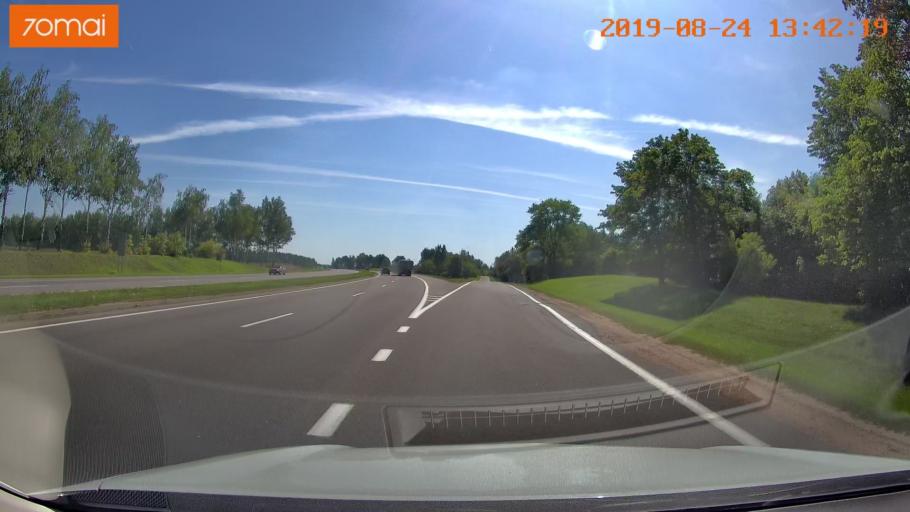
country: BY
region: Minsk
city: Samakhvalavichy
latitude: 53.7109
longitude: 27.5188
